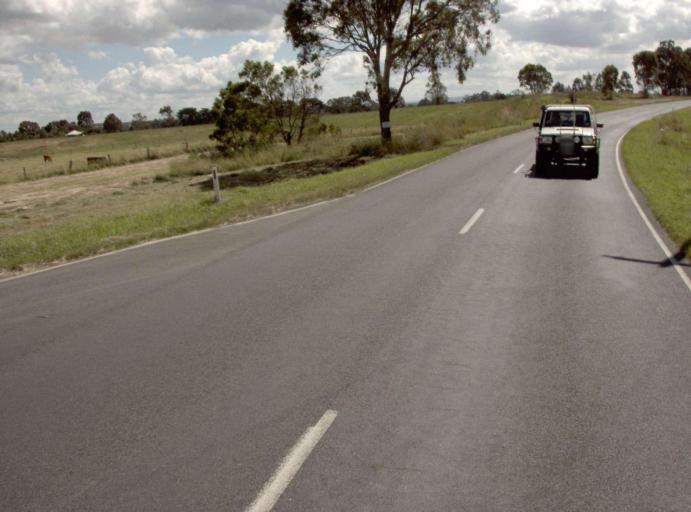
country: AU
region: Victoria
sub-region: Latrobe
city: Traralgon
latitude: -38.1537
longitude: 146.5188
